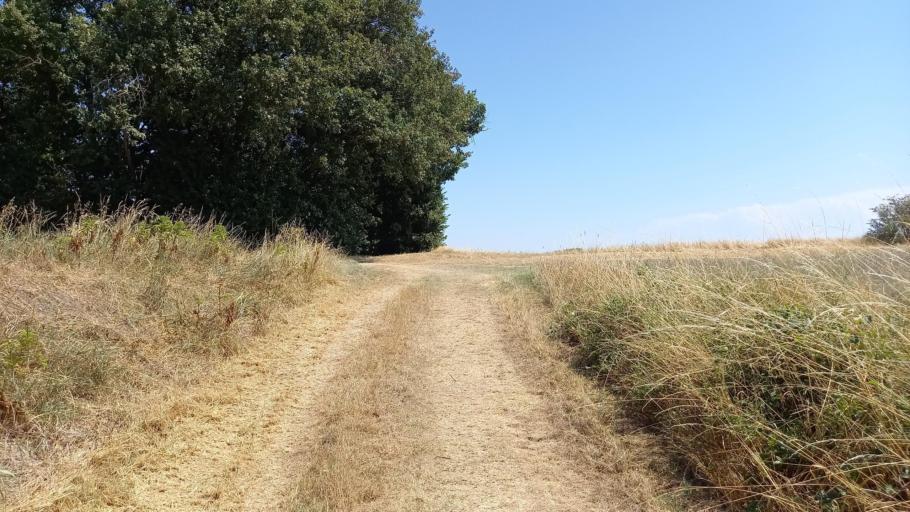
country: FR
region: Midi-Pyrenees
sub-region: Departement de la Haute-Garonne
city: Venerque
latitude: 43.4412
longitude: 1.4428
